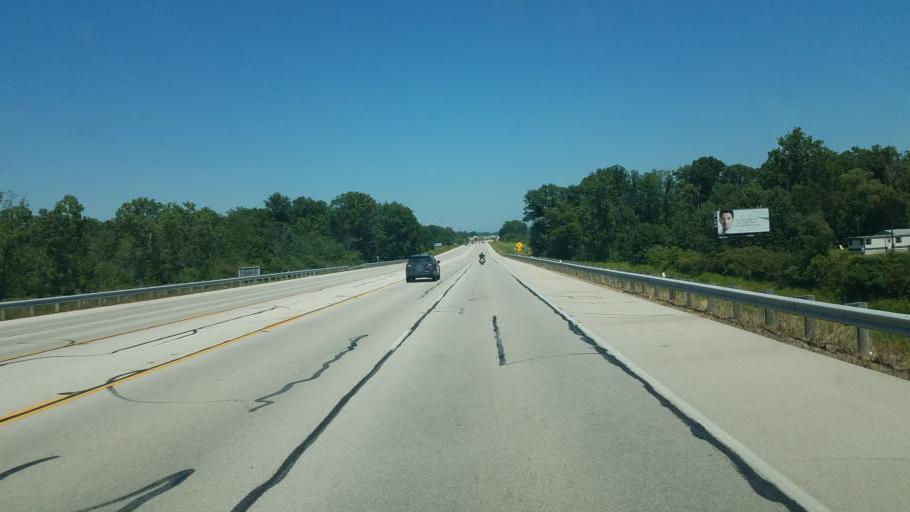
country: US
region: Ohio
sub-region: Sandusky County
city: Fremont
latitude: 41.3860
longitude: -83.1142
